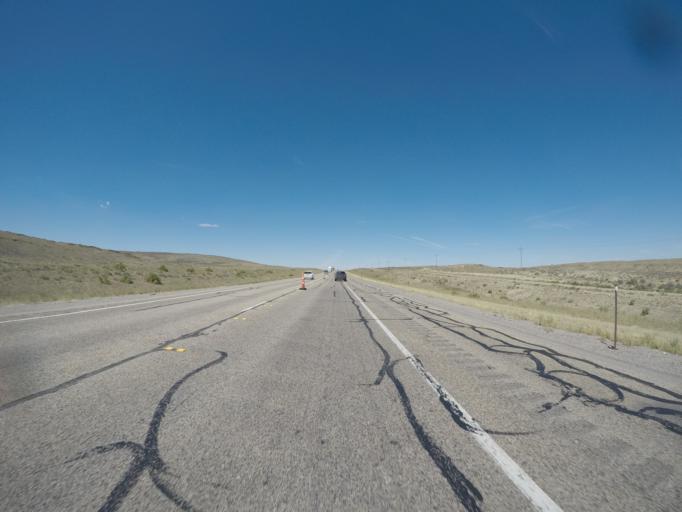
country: US
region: Wyoming
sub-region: Carbon County
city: Saratoga
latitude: 41.7429
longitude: -106.8658
